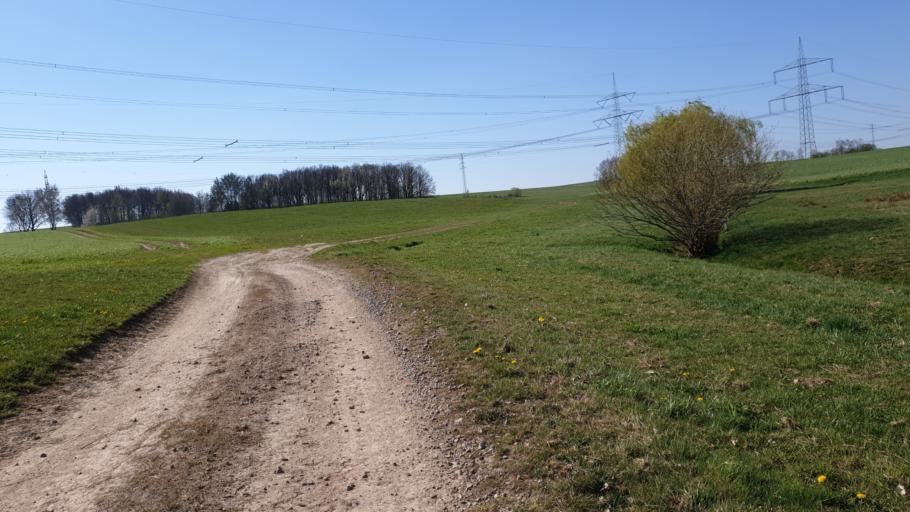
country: DE
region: Saxony
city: Claussnitz
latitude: 50.9346
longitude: 12.9070
